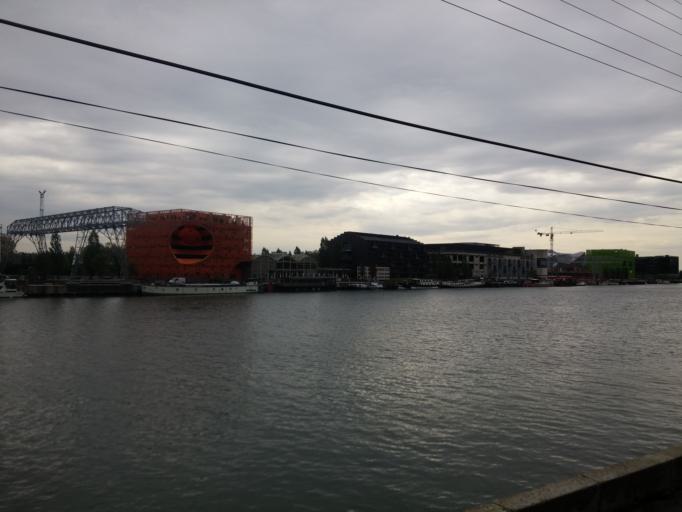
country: FR
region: Rhone-Alpes
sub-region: Departement du Rhone
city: La Mulatiere
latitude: 45.7400
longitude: 4.8121
